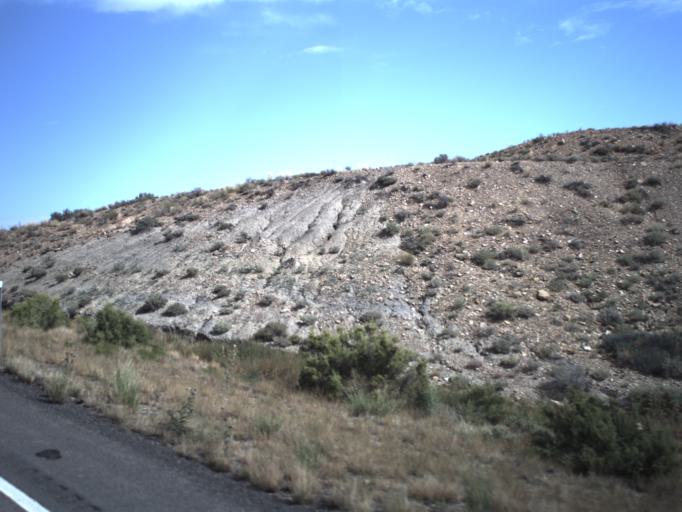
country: US
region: Utah
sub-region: Carbon County
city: East Carbon City
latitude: 39.5000
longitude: -110.5269
